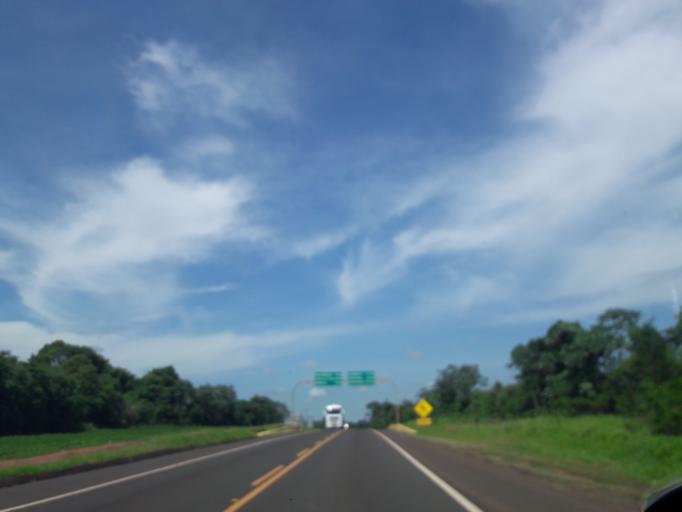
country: BR
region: Parana
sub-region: Campo Mourao
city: Campo Mourao
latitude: -24.2801
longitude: -52.5362
